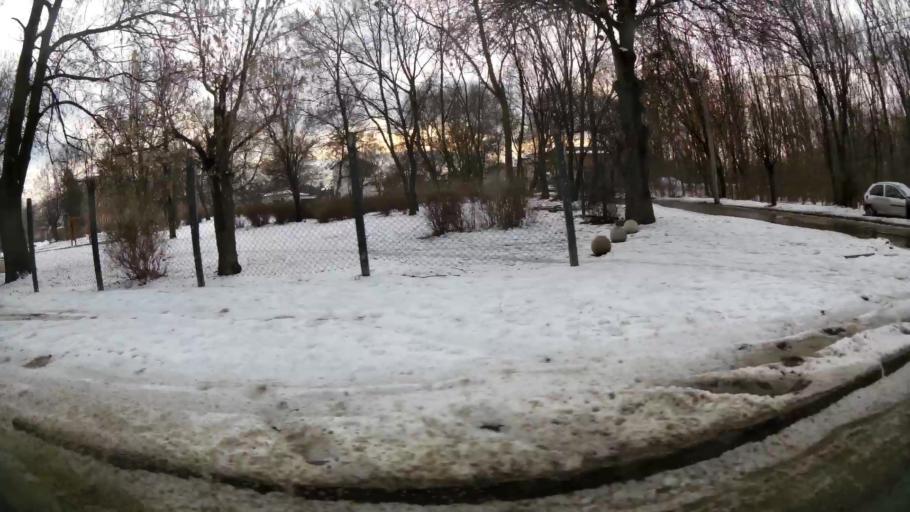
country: BG
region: Sofia-Capital
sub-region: Stolichna Obshtina
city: Sofia
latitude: 42.7270
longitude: 23.3394
